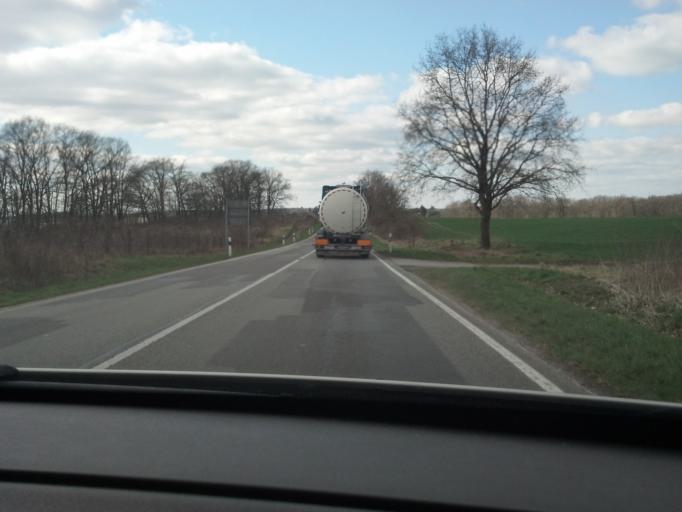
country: DE
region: Mecklenburg-Vorpommern
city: Malchow
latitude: 53.3696
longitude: 12.3639
